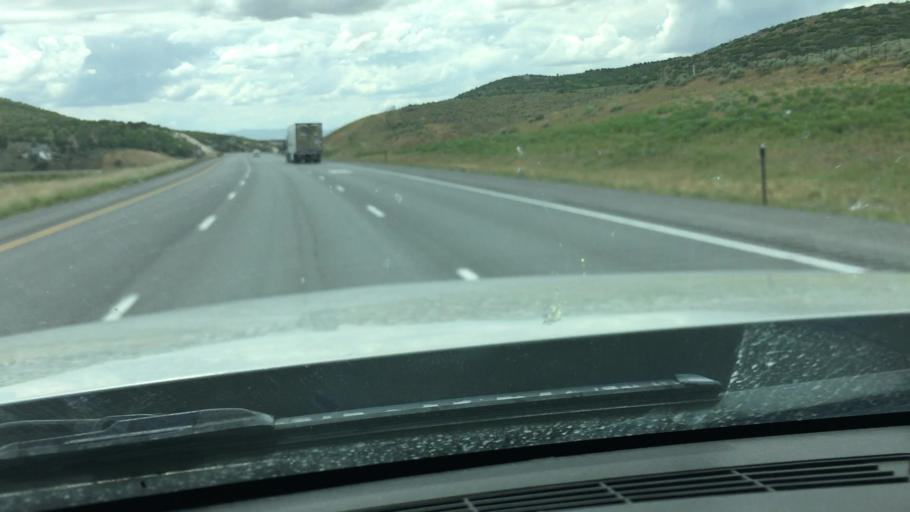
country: US
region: Utah
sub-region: Beaver County
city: Beaver
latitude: 38.4640
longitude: -112.6197
